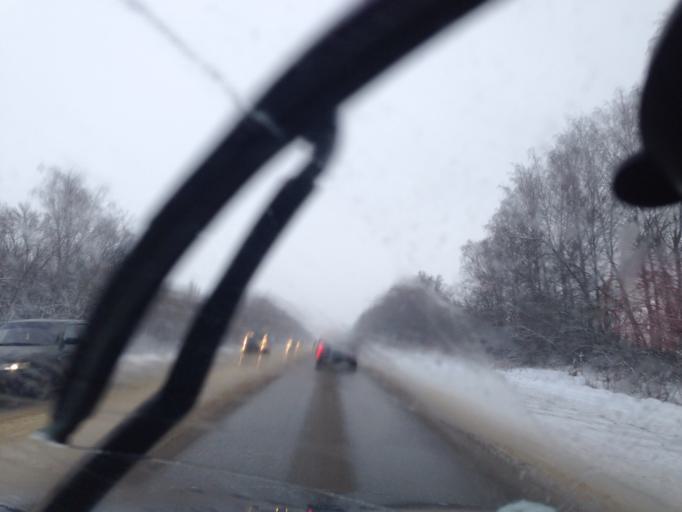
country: RU
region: Tula
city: Bolokhovo
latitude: 54.0951
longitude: 37.7690
